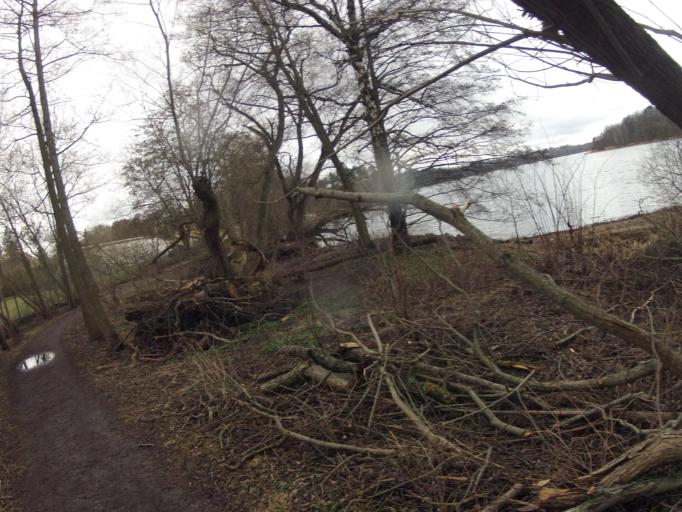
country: SE
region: Stockholm
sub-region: Norrtalje Kommun
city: Bergshamra
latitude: 59.3722
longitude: 18.0478
